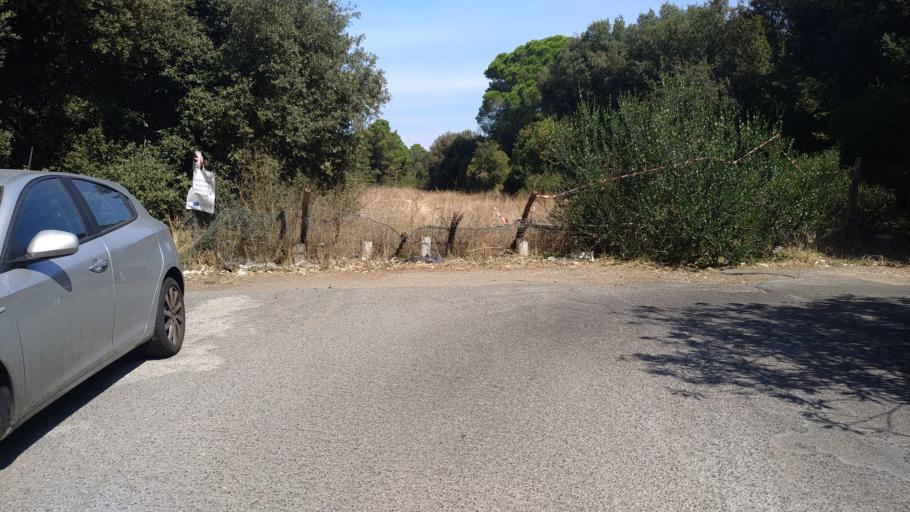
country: IT
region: Latium
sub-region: Citta metropolitana di Roma Capitale
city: Lido di Ostia
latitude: 41.7321
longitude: 12.3035
